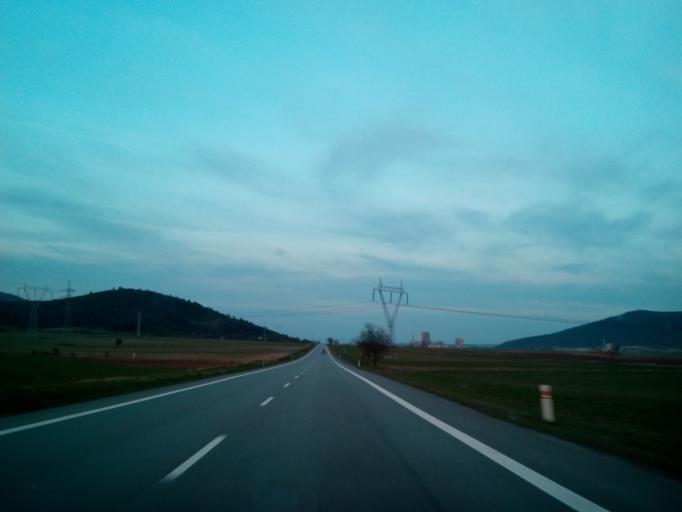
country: SK
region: Kosicky
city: Medzev
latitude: 48.6002
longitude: 20.7901
